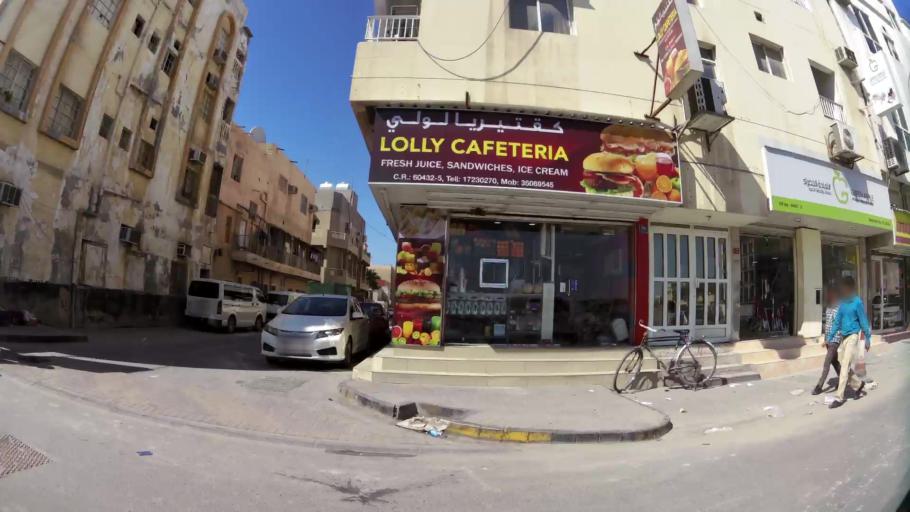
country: BH
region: Manama
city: Manama
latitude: 26.2169
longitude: 50.5688
